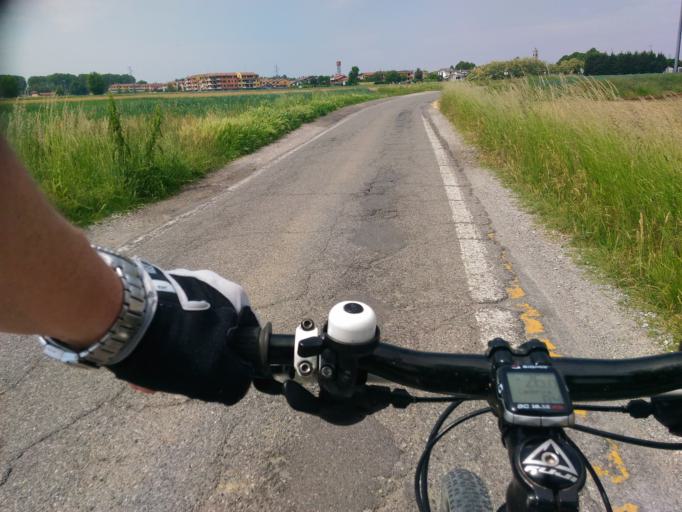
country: IT
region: Lombardy
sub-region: Provincia di Lodi
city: Casalmaiocco
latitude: 45.3504
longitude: 9.3819
